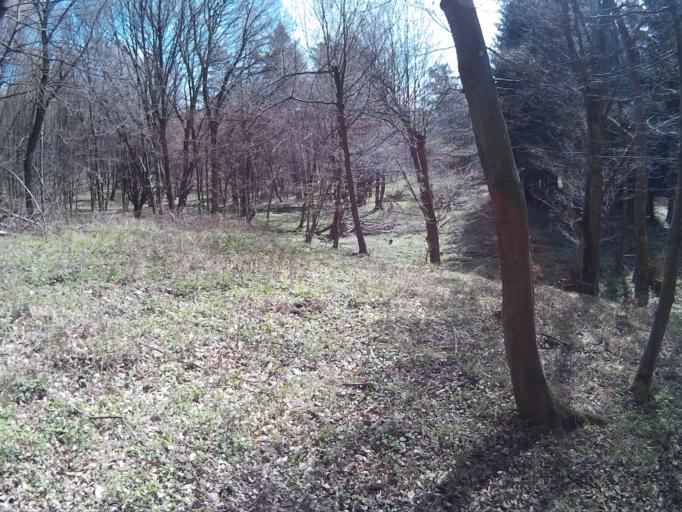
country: HU
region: Veszprem
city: Herend
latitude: 47.2063
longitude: 17.7748
